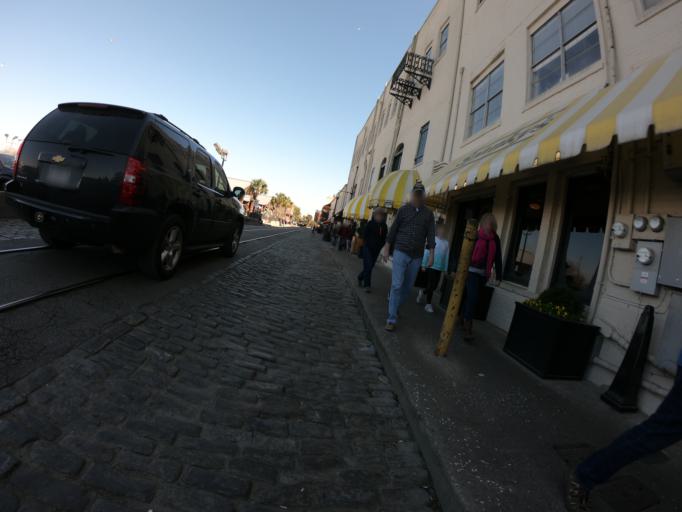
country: US
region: Georgia
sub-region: Chatham County
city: Savannah
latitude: 32.0806
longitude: -81.0867
